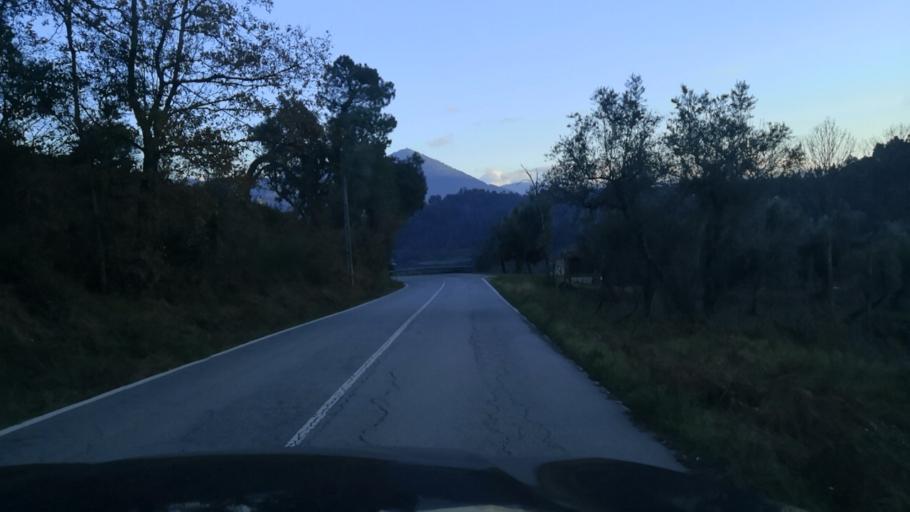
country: PT
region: Vila Real
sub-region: Mondim de Basto
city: Mondim de Basto
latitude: 41.4619
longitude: -7.9599
